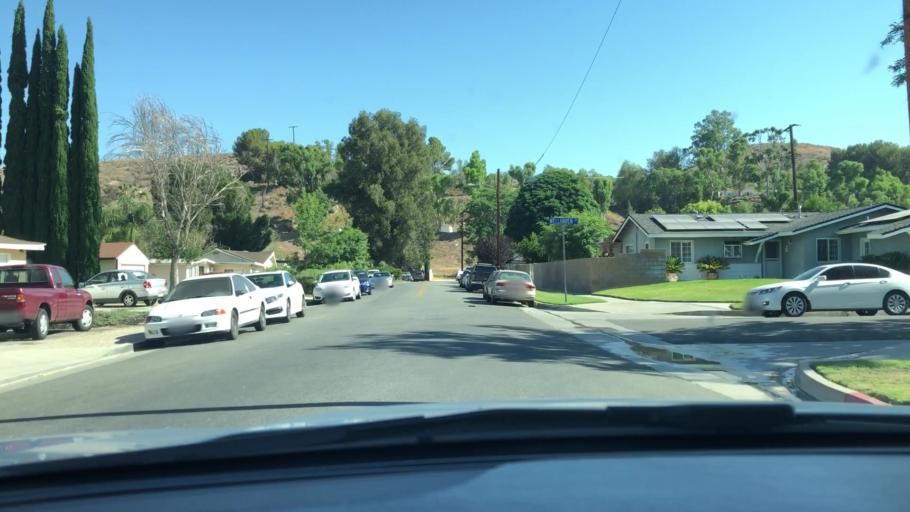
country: US
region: California
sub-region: Los Angeles County
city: Santa Clarita
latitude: 34.4175
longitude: -118.4472
